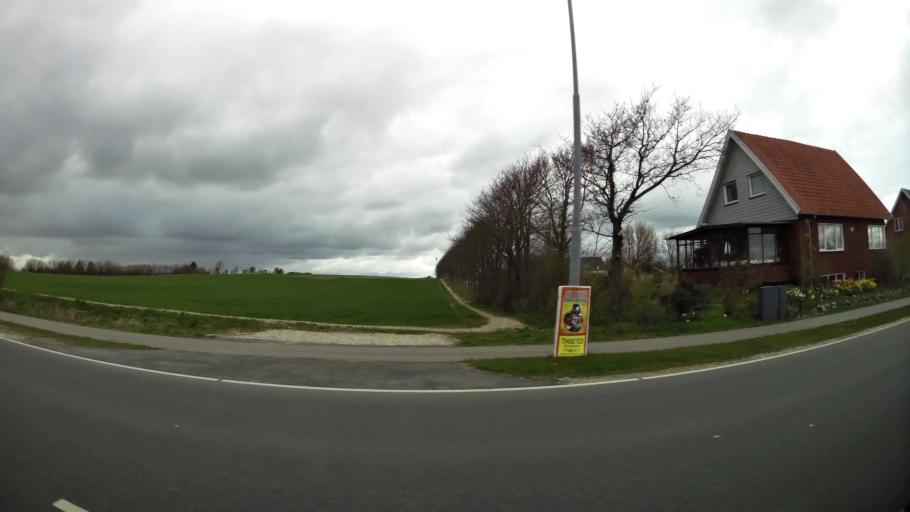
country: DK
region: North Denmark
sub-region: Thisted Kommune
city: Thisted
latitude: 56.9449
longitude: 8.6575
